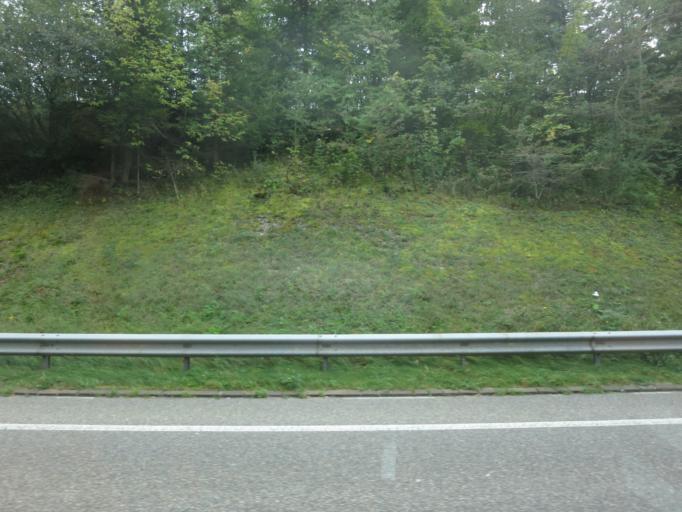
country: CH
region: Zurich
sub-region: Bezirk Hinwil
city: Rueti / Westlicher Dorfteil
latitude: 47.2468
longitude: 8.8401
